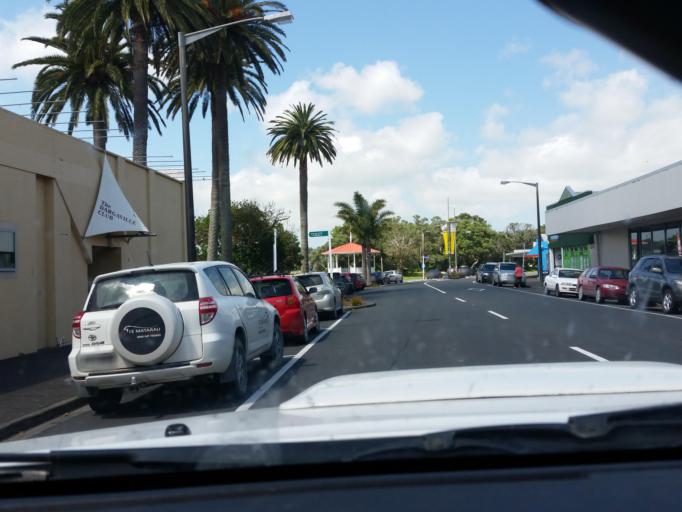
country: NZ
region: Northland
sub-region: Kaipara District
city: Dargaville
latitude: -35.9425
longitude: 173.8692
